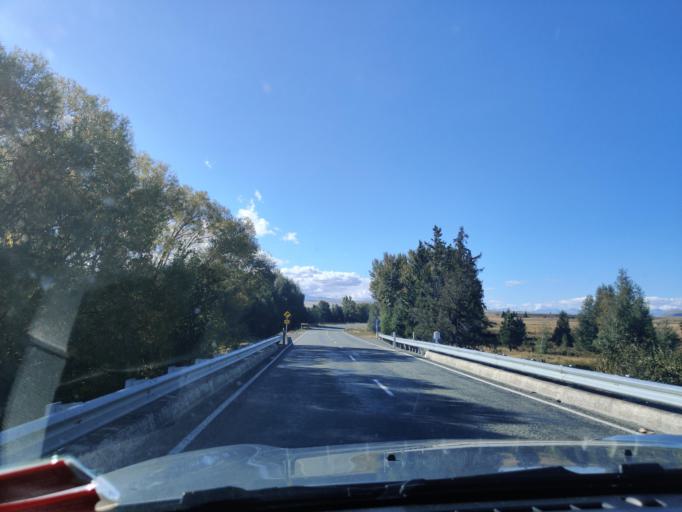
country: NZ
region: Canterbury
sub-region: Timaru District
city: Pleasant Point
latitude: -44.0875
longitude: 170.3489
